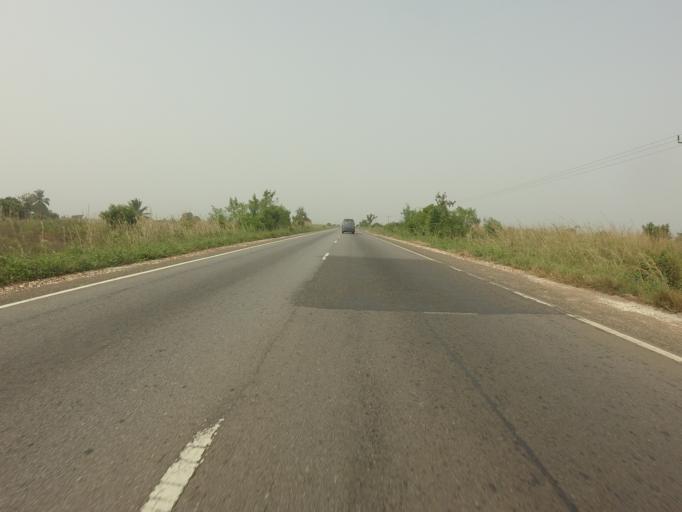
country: GH
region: Volta
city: Anloga
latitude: 5.9150
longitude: 0.5228
